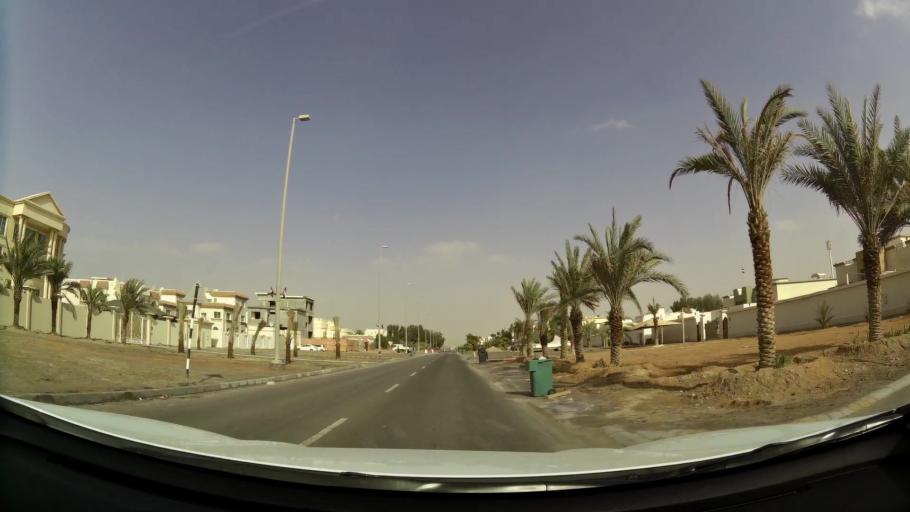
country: AE
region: Abu Dhabi
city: Abu Dhabi
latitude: 24.4117
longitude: 54.5812
